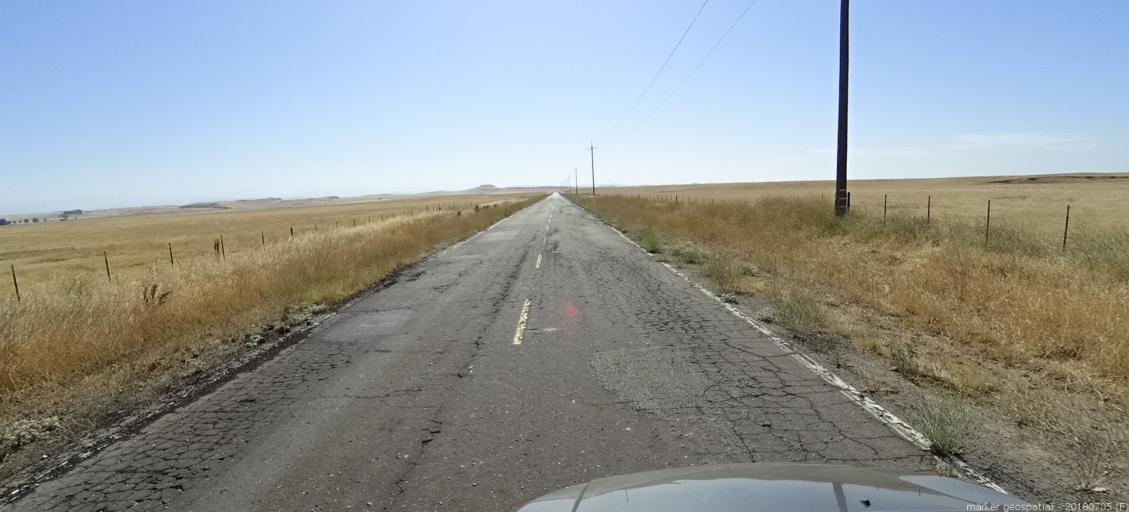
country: US
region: California
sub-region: Madera County
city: Madera Acres
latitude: 37.1268
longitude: -120.0359
